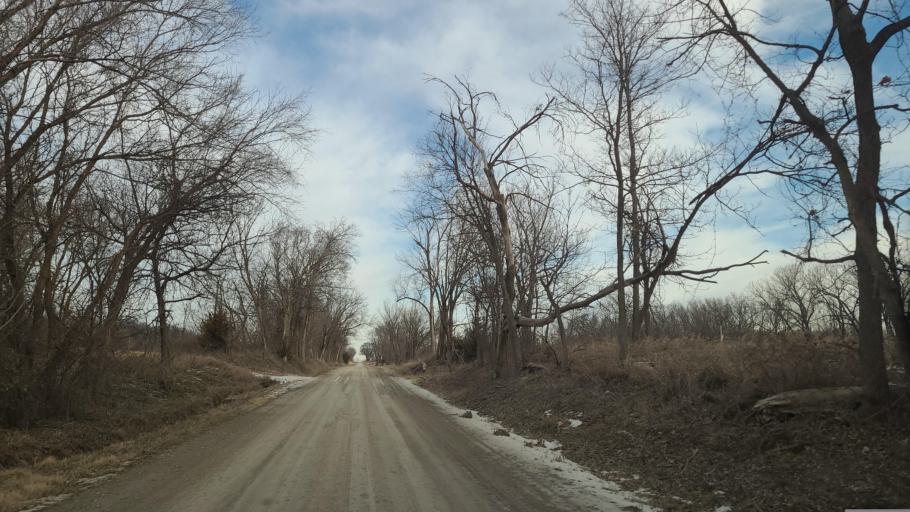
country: US
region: Kansas
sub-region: Douglas County
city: Lawrence
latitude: 39.0464
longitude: -95.4098
